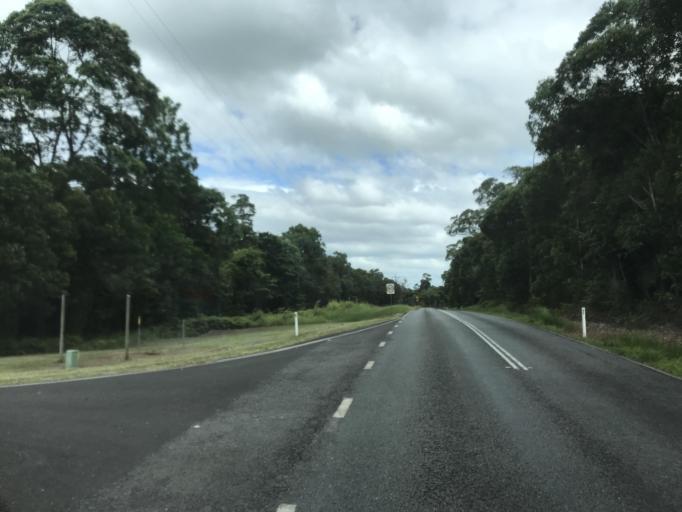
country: AU
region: Queensland
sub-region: Cassowary Coast
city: Innisfail
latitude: -17.8415
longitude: 146.0544
